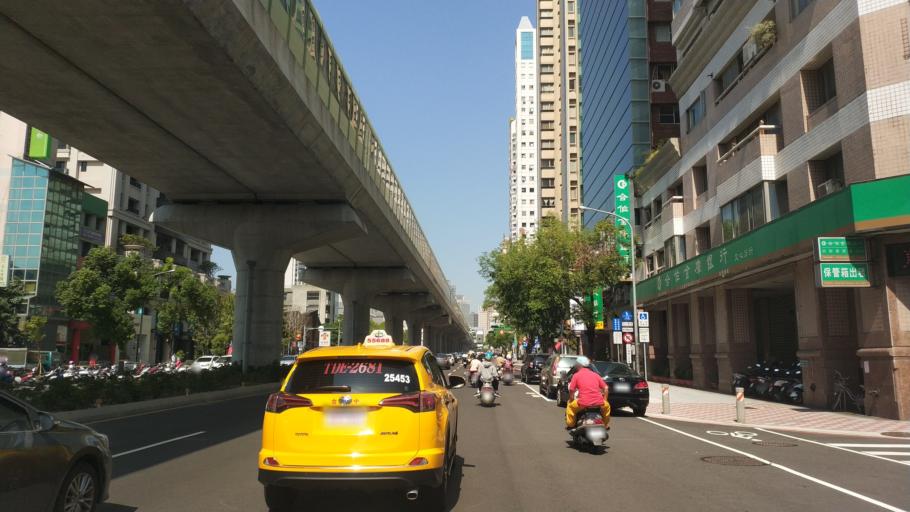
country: TW
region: Taiwan
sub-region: Taichung City
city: Taichung
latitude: 24.1477
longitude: 120.6468
